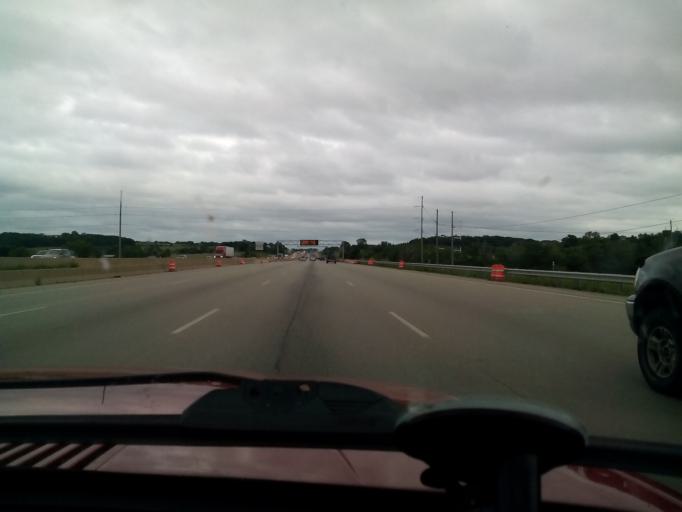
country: US
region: Wisconsin
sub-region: Dane County
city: Monona
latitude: 43.1262
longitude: -89.2911
